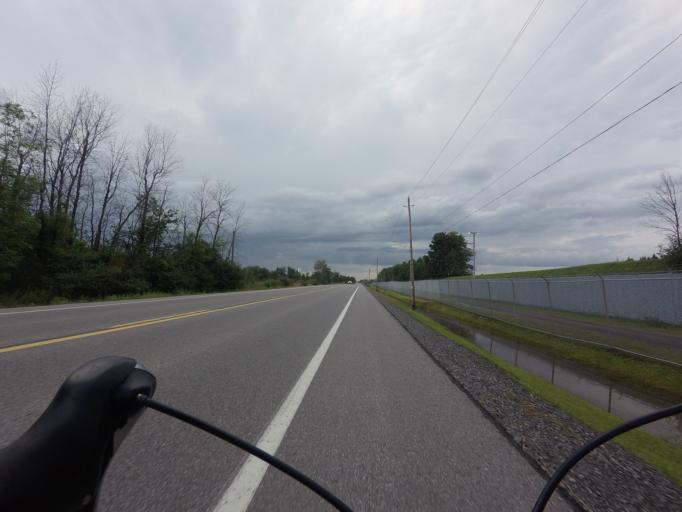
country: CA
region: Ontario
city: Carleton Place
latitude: 45.1296
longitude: -75.9484
